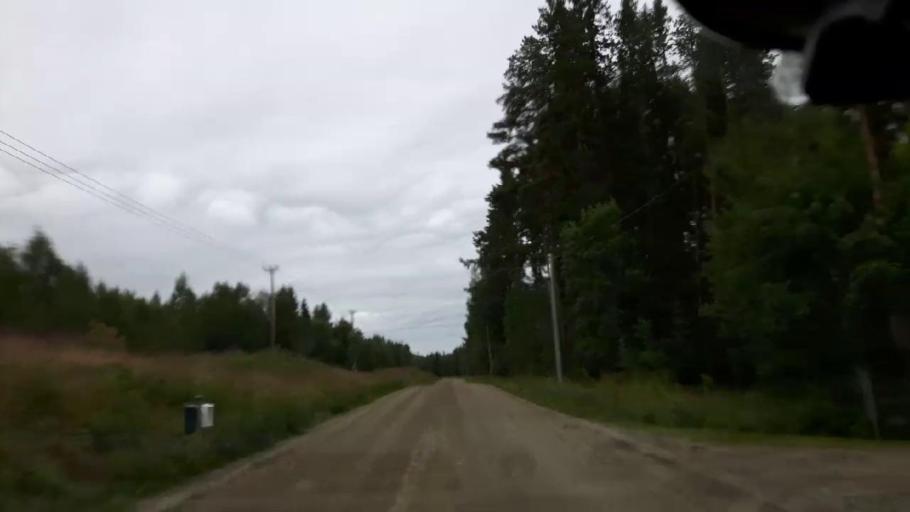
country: SE
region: Jaemtland
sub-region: Braecke Kommun
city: Braecke
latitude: 63.0234
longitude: 15.3727
